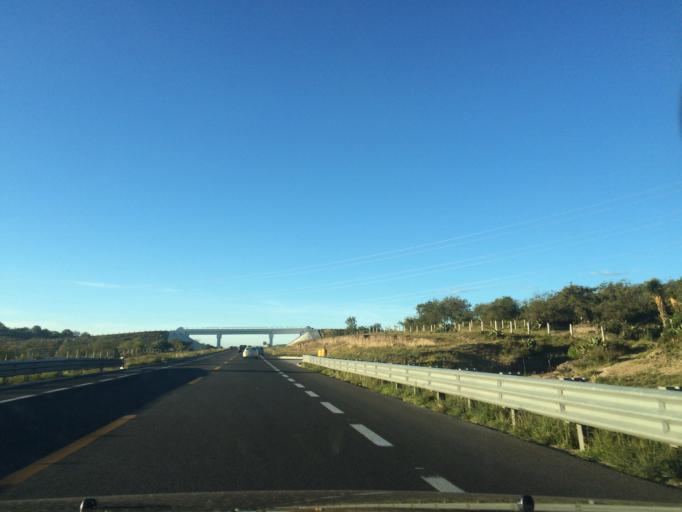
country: MX
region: Puebla
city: Morelos Canada
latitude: 18.7051
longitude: -97.4673
